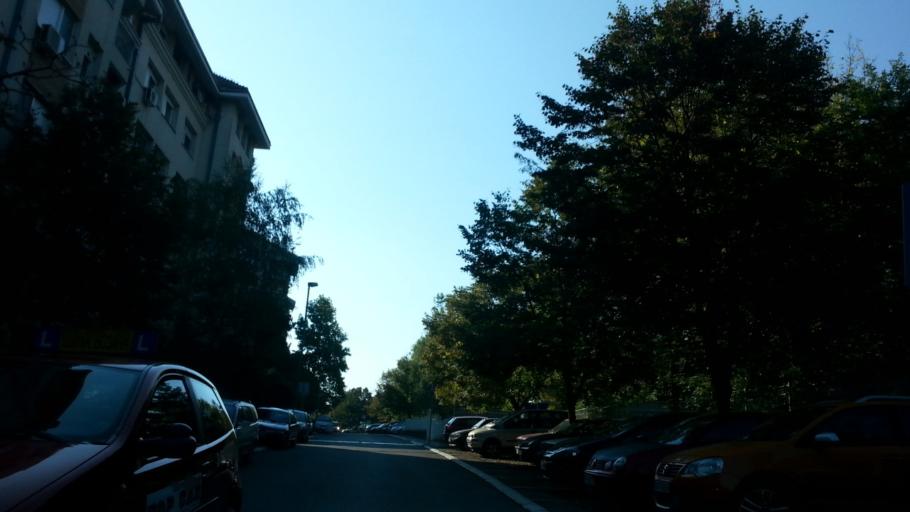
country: RS
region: Central Serbia
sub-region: Belgrade
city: Cukarica
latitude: 44.7687
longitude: 20.4149
